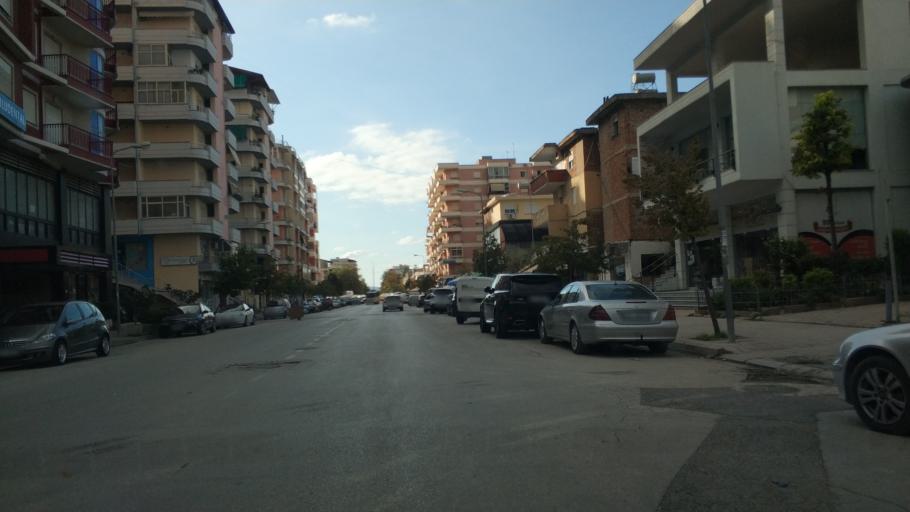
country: AL
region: Vlore
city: Vlore
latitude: 40.4614
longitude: 19.4854
